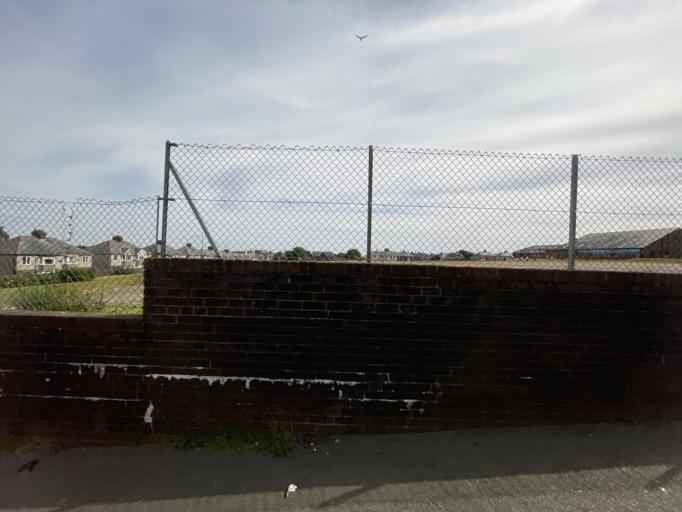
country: GB
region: Wales
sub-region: Gwynedd
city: Bangor
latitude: 53.2205
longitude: -4.1477
